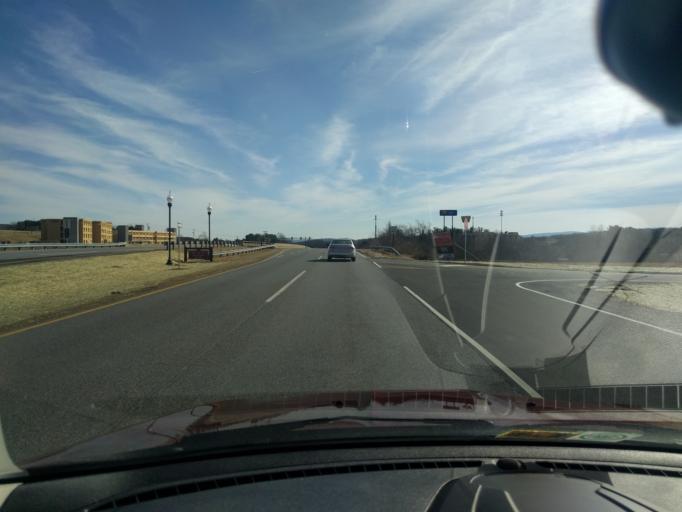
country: US
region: Virginia
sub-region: City of Staunton
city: Staunton
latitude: 38.1323
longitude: -79.0409
